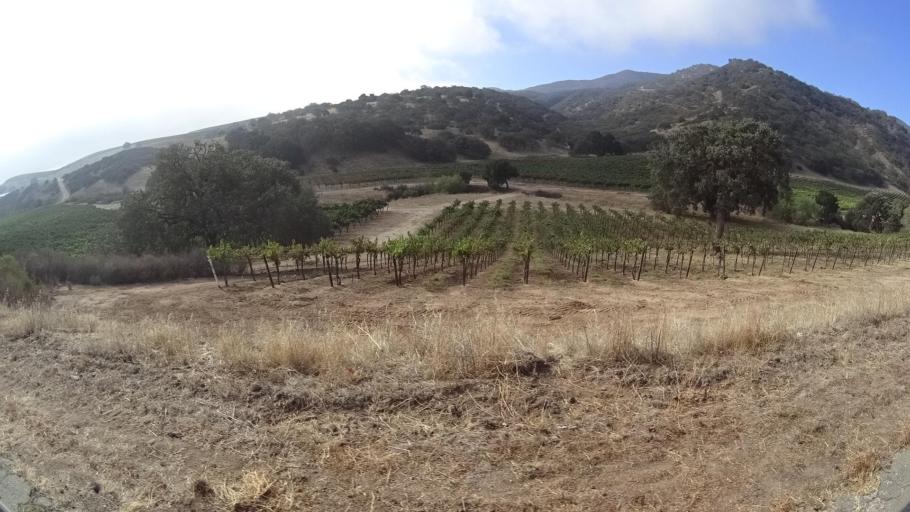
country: US
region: California
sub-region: Monterey County
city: Soledad
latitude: 36.3366
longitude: -121.3502
